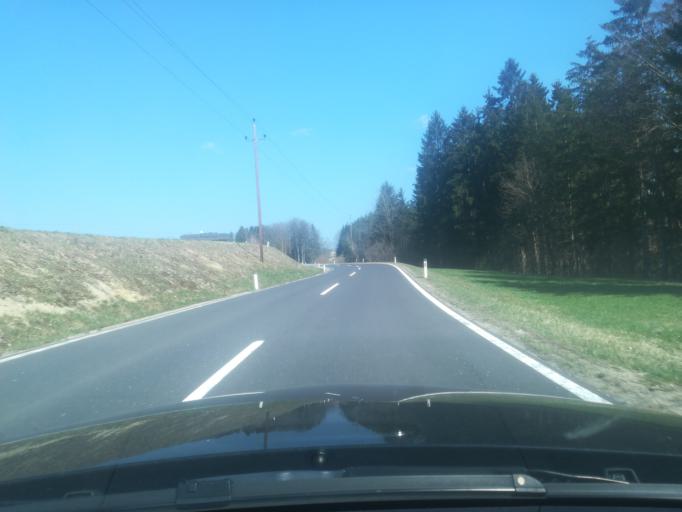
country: AT
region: Upper Austria
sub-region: Politischer Bezirk Perg
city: Perg
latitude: 48.3633
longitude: 14.6808
